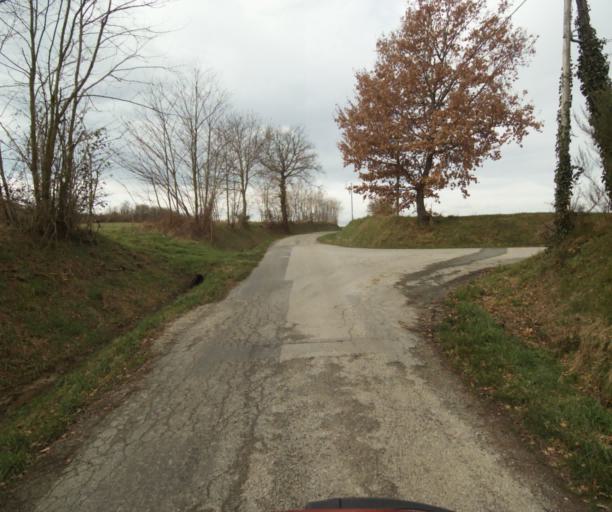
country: FR
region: Midi-Pyrenees
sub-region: Departement de l'Ariege
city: Verniolle
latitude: 43.0833
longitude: 1.7040
